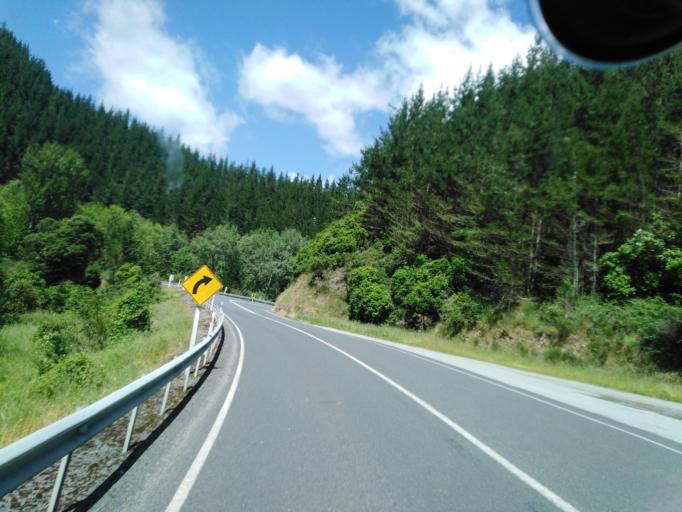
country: NZ
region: Nelson
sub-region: Nelson City
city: Nelson
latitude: -41.2273
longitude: 173.4054
